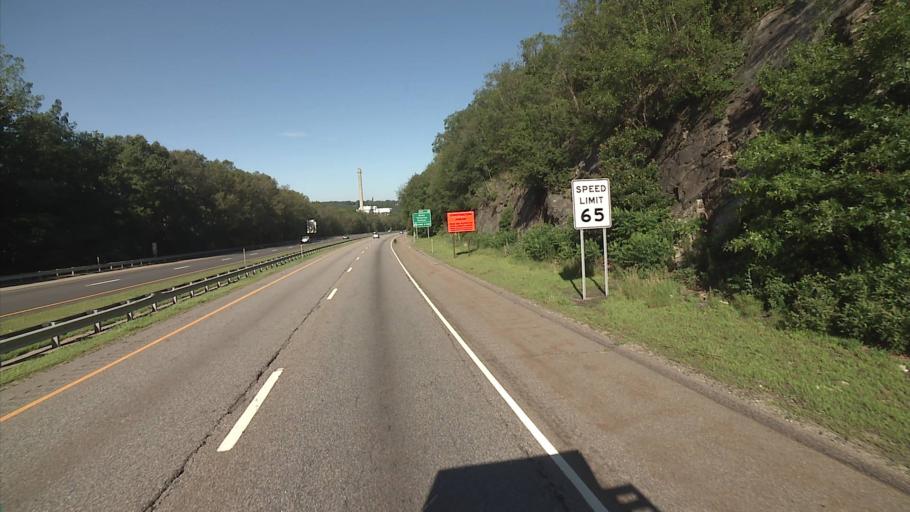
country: US
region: Connecticut
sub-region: New London County
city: Lisbon
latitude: 41.5864
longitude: -72.0334
